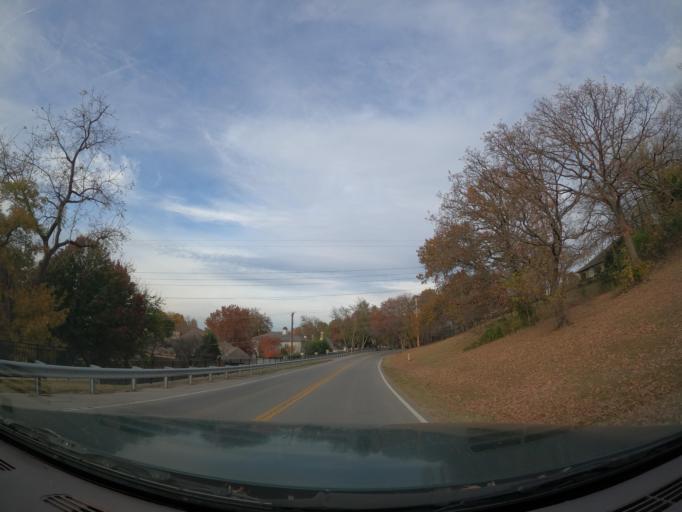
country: US
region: Oklahoma
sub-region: Tulsa County
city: Jenks
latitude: 36.0531
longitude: -95.9411
